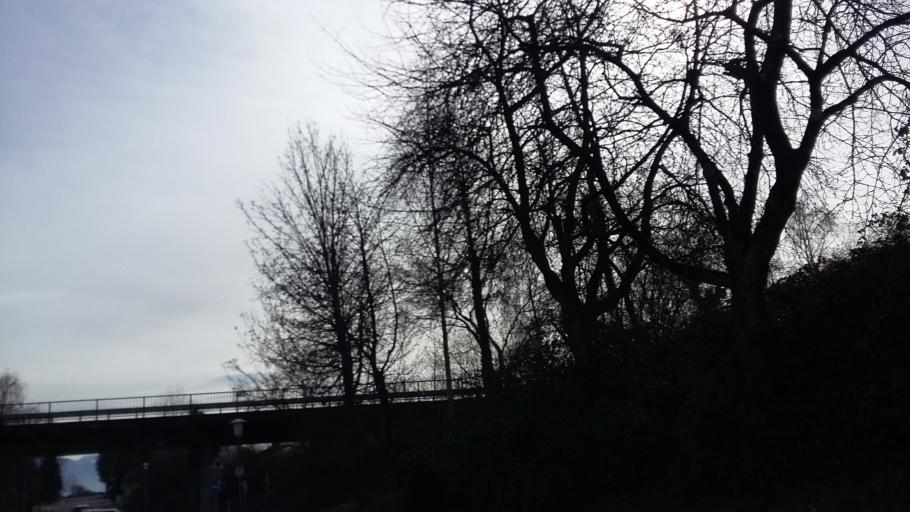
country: DE
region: Bavaria
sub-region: Swabia
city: Nonnenhorn
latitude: 47.5749
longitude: 9.6350
